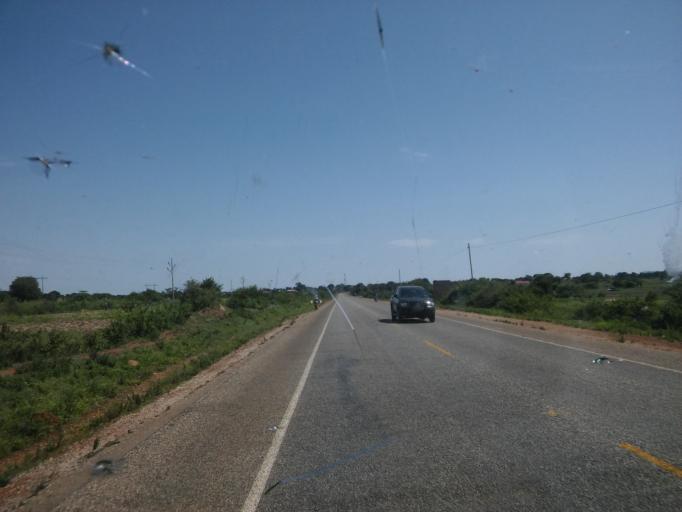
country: UG
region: Eastern Region
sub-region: Kumi District
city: Kumi
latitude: 1.4713
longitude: 33.9487
